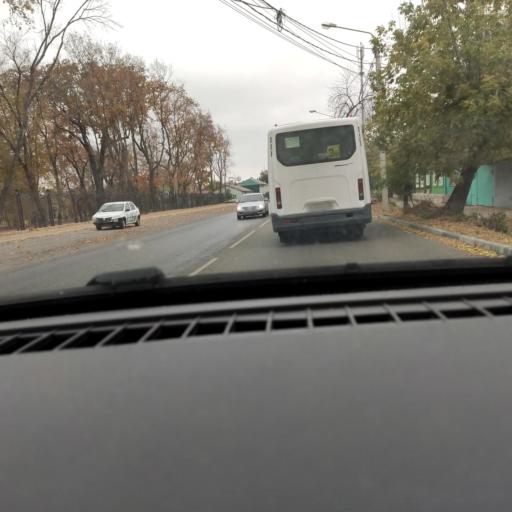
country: RU
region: Voronezj
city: Voronezh
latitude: 51.6838
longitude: 39.2128
